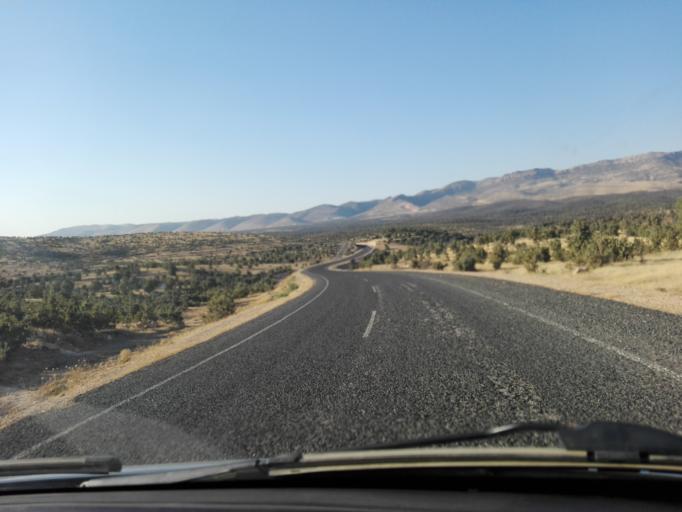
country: TR
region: Mardin
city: Kilavuz
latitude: 37.5033
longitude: 41.7621
